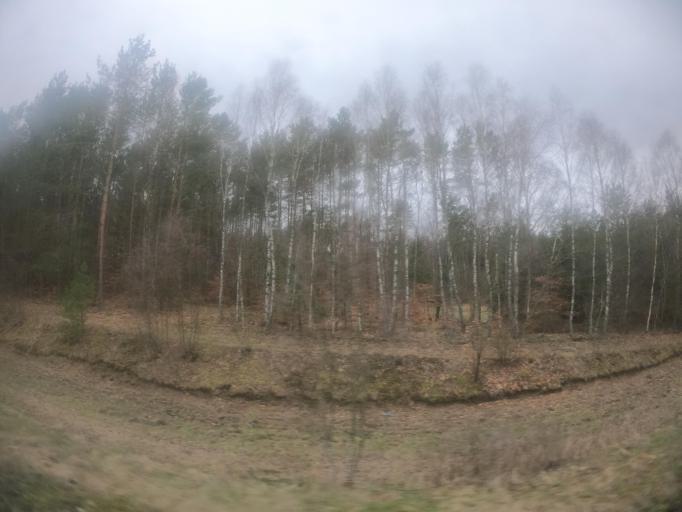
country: PL
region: West Pomeranian Voivodeship
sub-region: Powiat szczecinecki
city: Bialy Bor
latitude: 53.8014
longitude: 16.8647
